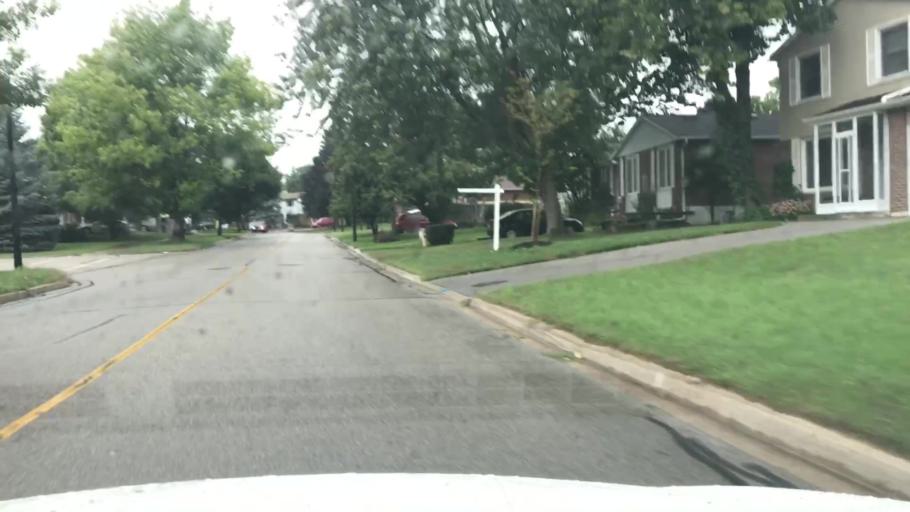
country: CA
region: Ontario
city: Newmarket
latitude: 44.0417
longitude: -79.4647
